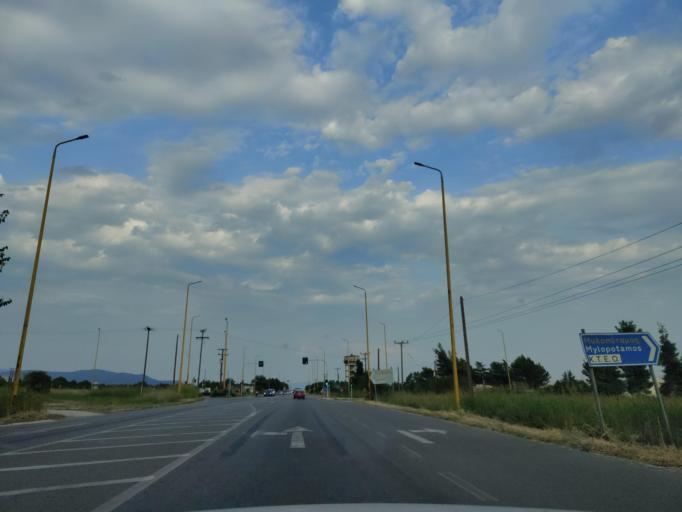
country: GR
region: East Macedonia and Thrace
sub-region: Nomos Dramas
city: Xiropotamos
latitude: 41.1635
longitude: 24.0706
